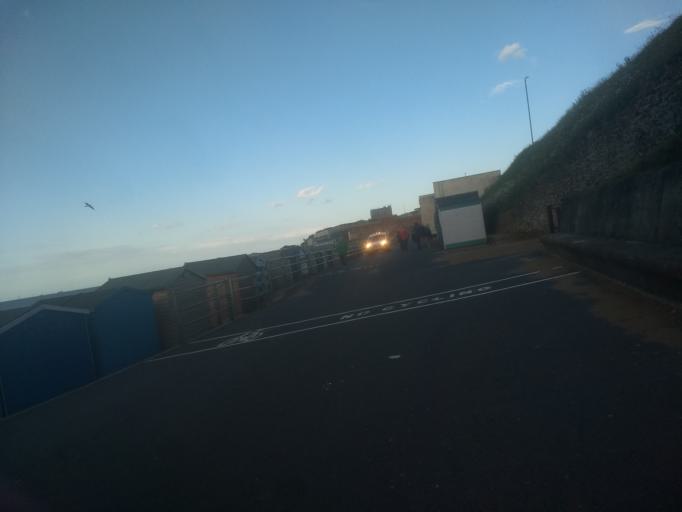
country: GB
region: England
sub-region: Kent
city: Westgate on Sea
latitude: 51.3854
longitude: 1.3613
